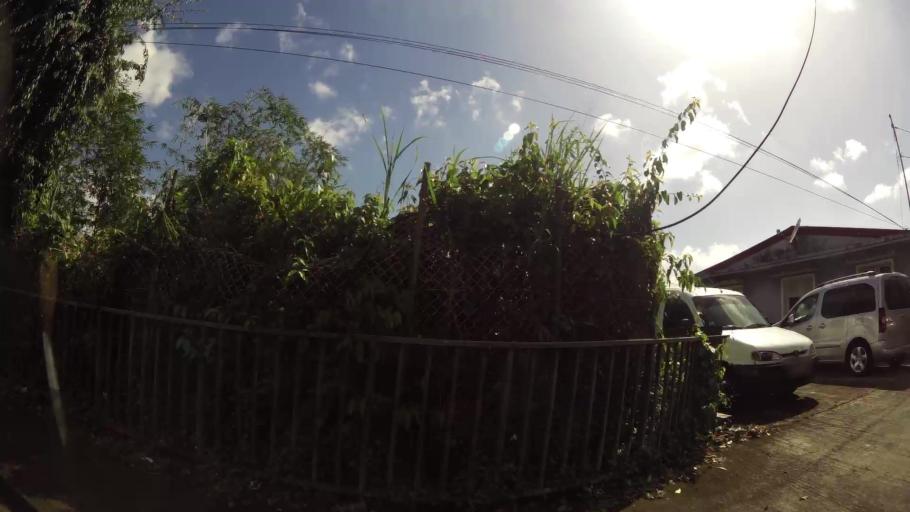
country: MQ
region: Martinique
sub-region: Martinique
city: Fort-de-France
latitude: 14.6223
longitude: -61.0540
